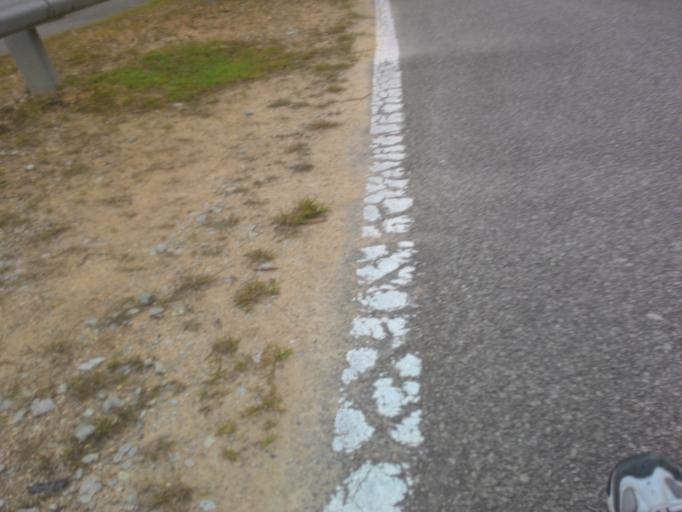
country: MY
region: Kedah
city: Kulim
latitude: 5.3805
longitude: 100.5777
